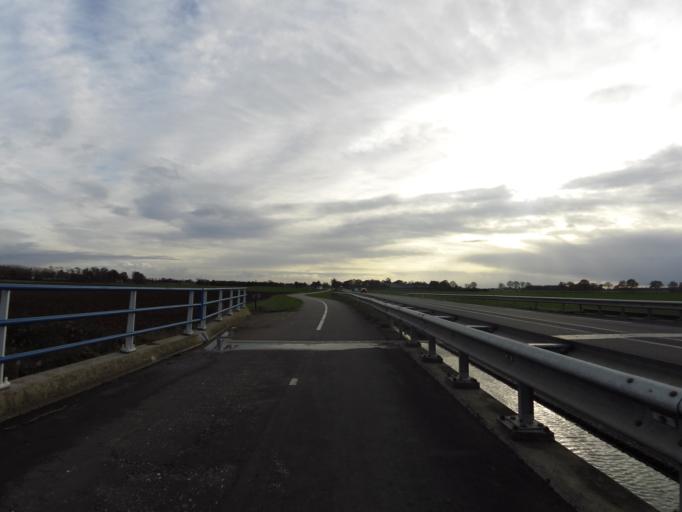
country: NL
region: Gelderland
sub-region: Gemeente Doetinchem
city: Doetinchem
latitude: 51.9362
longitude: 6.3142
